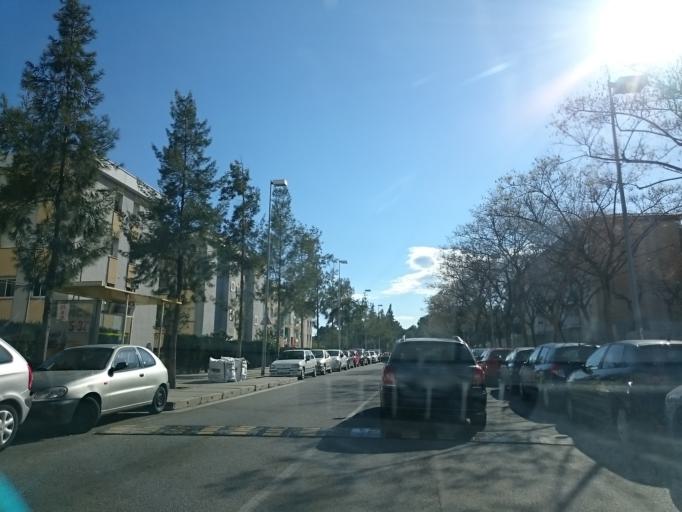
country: ES
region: Catalonia
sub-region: Provincia de Barcelona
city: Gava
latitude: 41.3089
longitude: 1.9924
